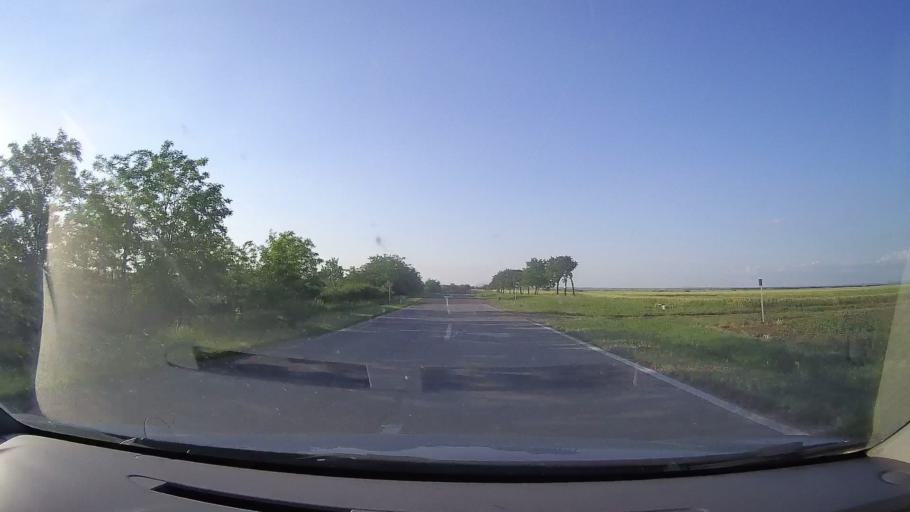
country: RO
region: Timis
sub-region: Comuna Moravita
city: Moravita
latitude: 45.2091
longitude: 21.2998
